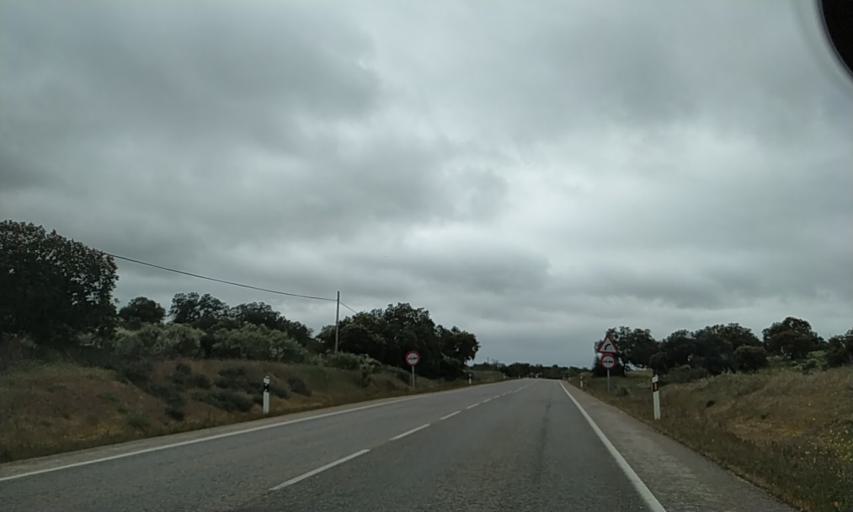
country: ES
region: Extremadura
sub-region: Provincia de Caceres
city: Caceres
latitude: 39.4021
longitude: -6.4212
